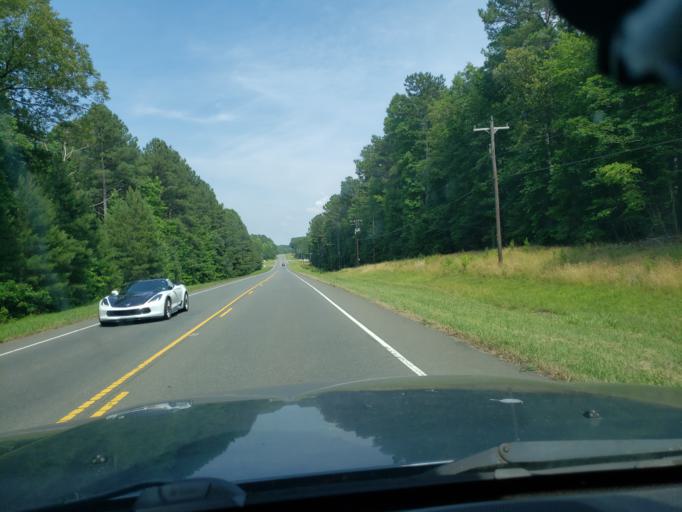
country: US
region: North Carolina
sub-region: Alamance County
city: Saxapahaw
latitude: 35.9330
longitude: -79.2220
